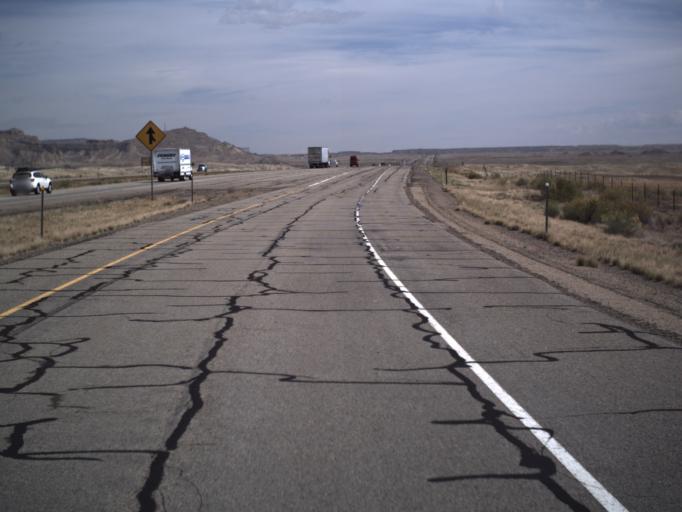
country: US
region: Utah
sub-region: Grand County
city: Moab
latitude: 38.9212
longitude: -109.9326
